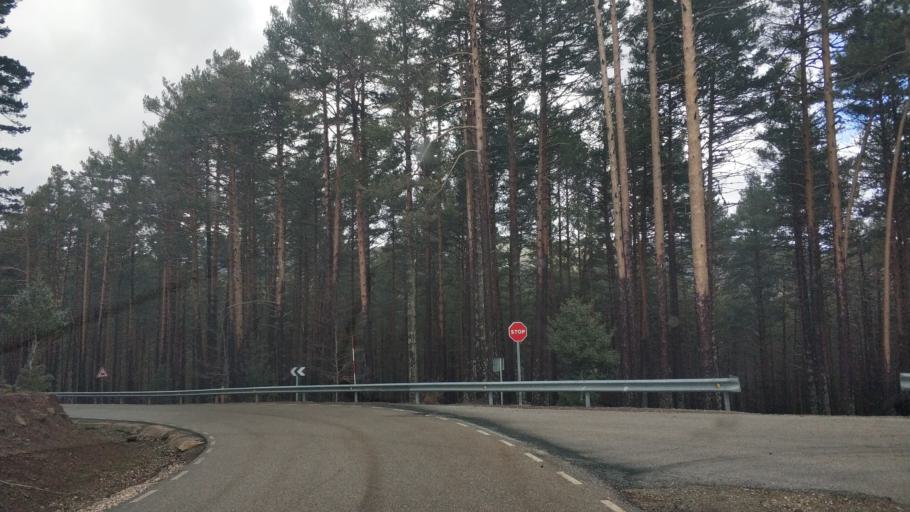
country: ES
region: Castille and Leon
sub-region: Provincia de Burgos
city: Neila
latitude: 42.0471
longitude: -3.0103
